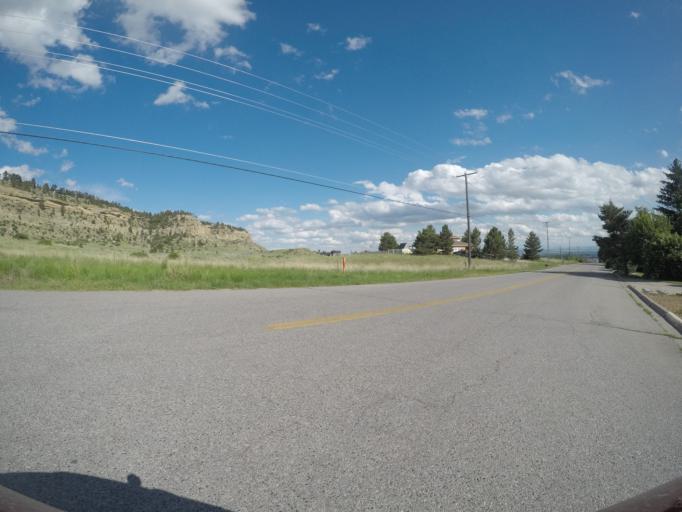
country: US
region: Montana
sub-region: Yellowstone County
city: Billings
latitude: 45.8078
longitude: -108.6528
